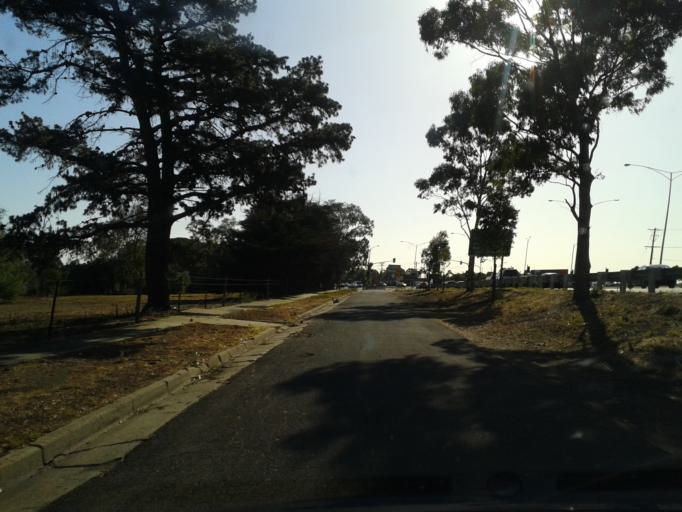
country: AU
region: Victoria
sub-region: Brimbank
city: Deer Park
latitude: -37.7707
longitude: 144.7921
